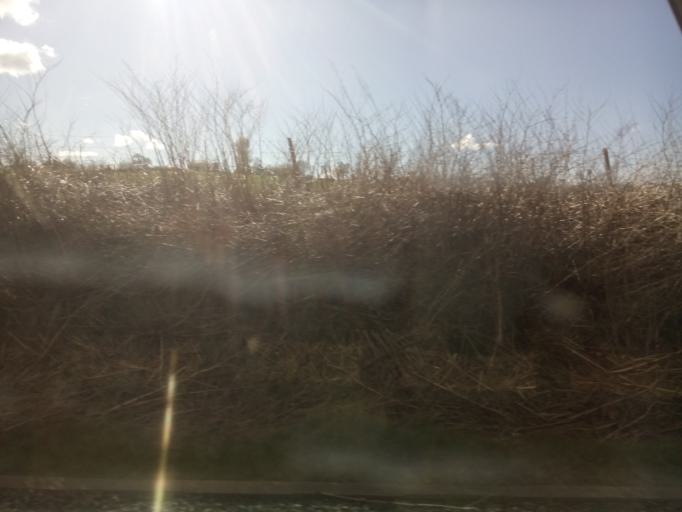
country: GB
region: England
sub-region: County Durham
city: Chester-le-Street
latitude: 54.8280
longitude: -1.5820
